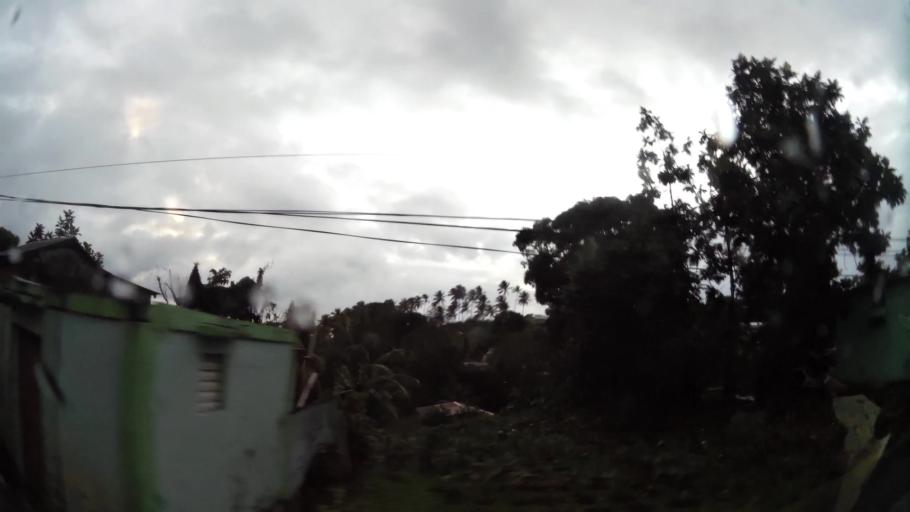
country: DM
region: Saint Andrew
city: Wesley
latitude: 15.5663
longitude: -61.3108
